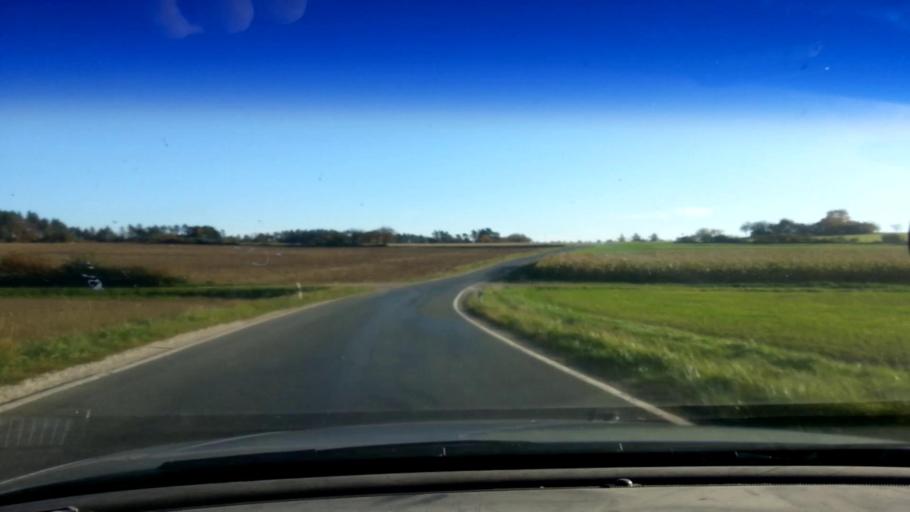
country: DE
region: Bavaria
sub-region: Upper Franconia
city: Poxdorf
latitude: 49.8996
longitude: 11.0926
